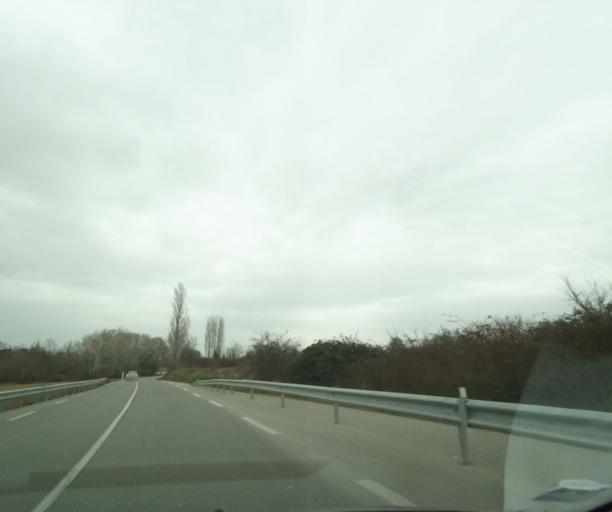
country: FR
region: Provence-Alpes-Cote d'Azur
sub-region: Departement des Bouches-du-Rhone
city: Eguilles
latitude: 43.5737
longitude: 5.3954
